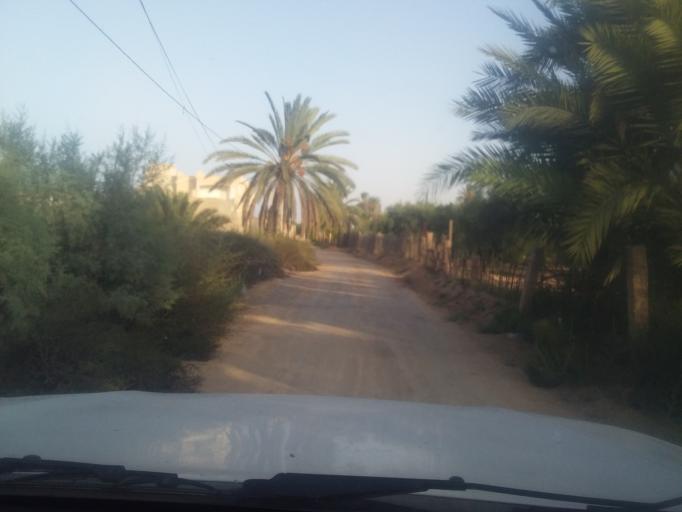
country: TN
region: Qabis
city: Gabes
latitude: 33.6292
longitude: 10.2887
